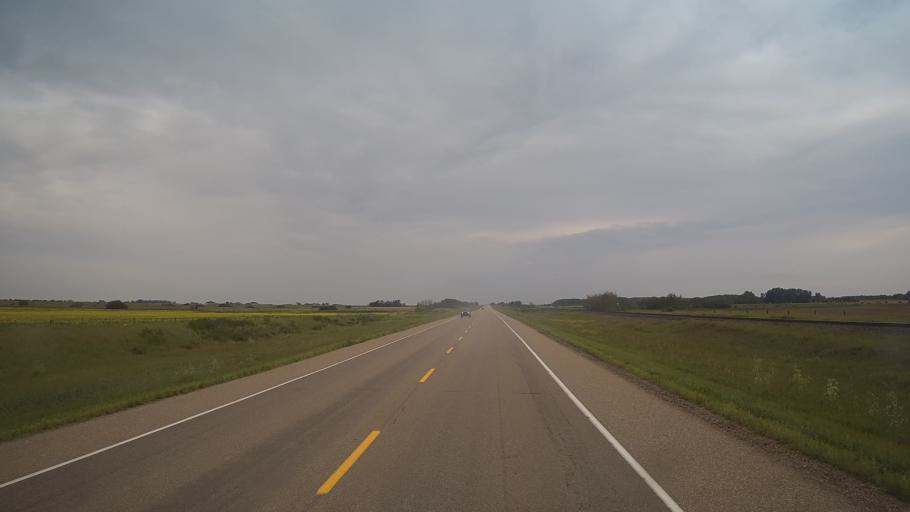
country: CA
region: Saskatchewan
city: Langham
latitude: 52.1273
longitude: -107.2587
